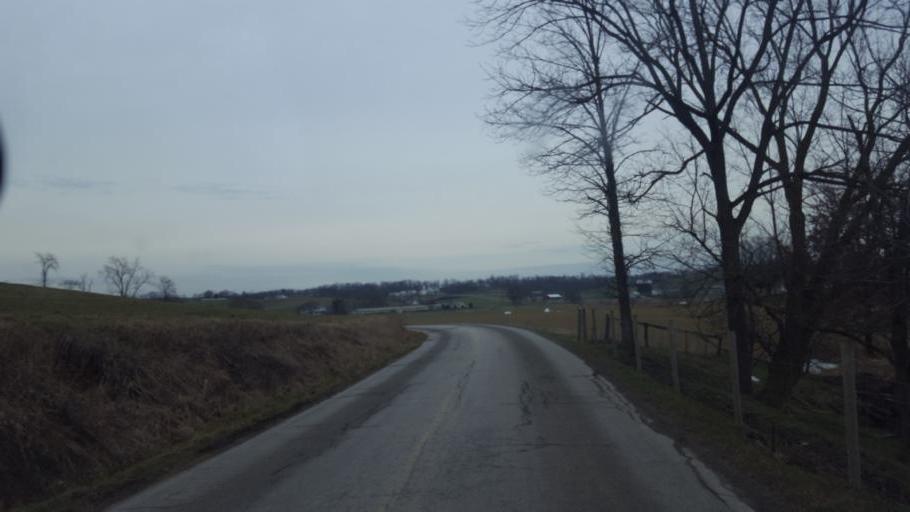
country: US
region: Ohio
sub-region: Tuscarawas County
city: Sugarcreek
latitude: 40.5124
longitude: -81.7333
